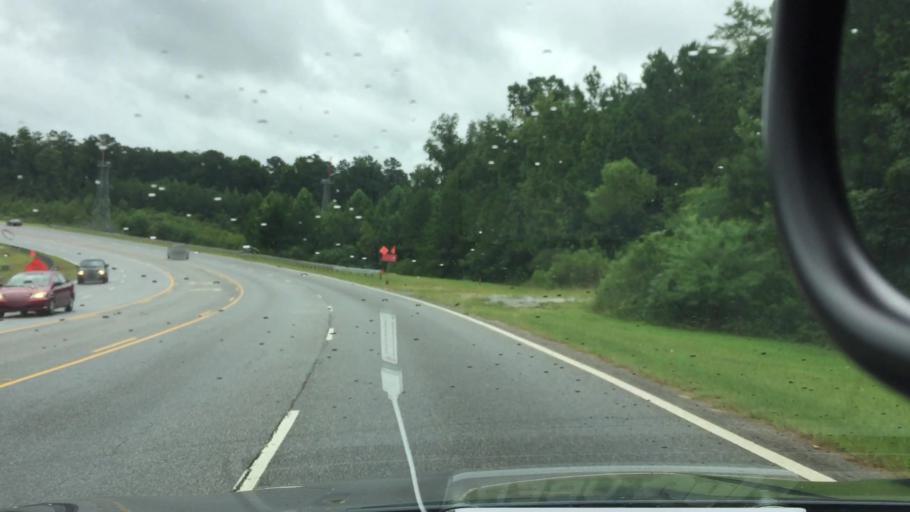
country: US
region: Alabama
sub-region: Lee County
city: Auburn
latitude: 32.6032
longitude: -85.4385
